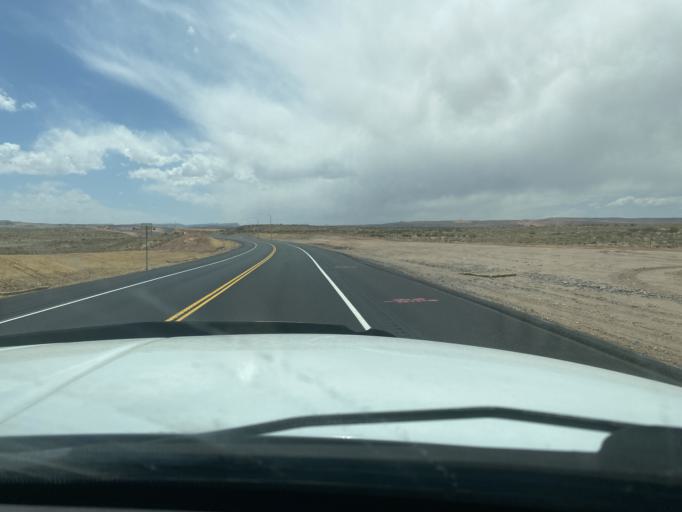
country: US
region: Utah
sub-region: Washington County
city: Hurricane
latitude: 37.1368
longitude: -113.3477
